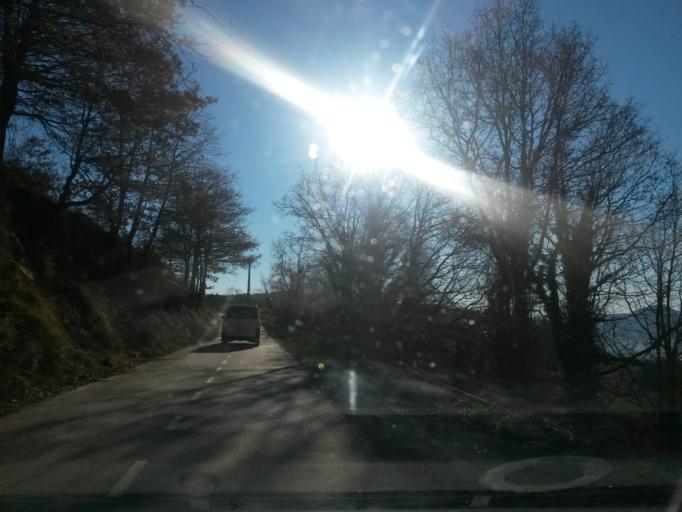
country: ES
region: Catalonia
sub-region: Provincia de Girona
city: les Planes d'Hostoles
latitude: 42.0389
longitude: 2.5152
